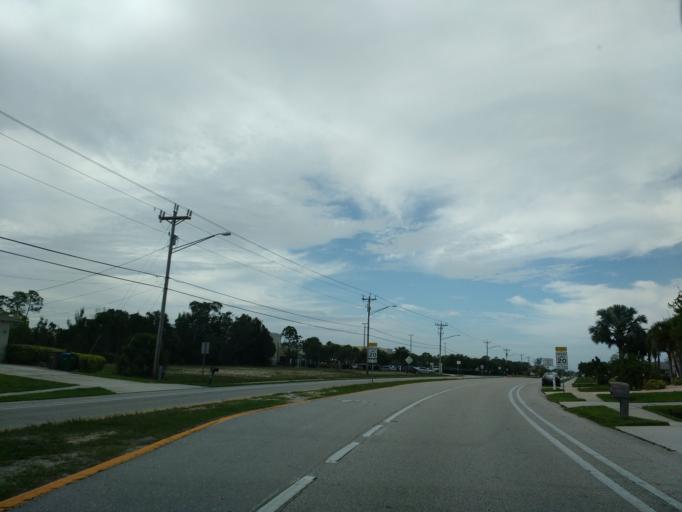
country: US
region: Florida
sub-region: Lee County
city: Cape Coral
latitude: 26.5898
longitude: -82.0241
